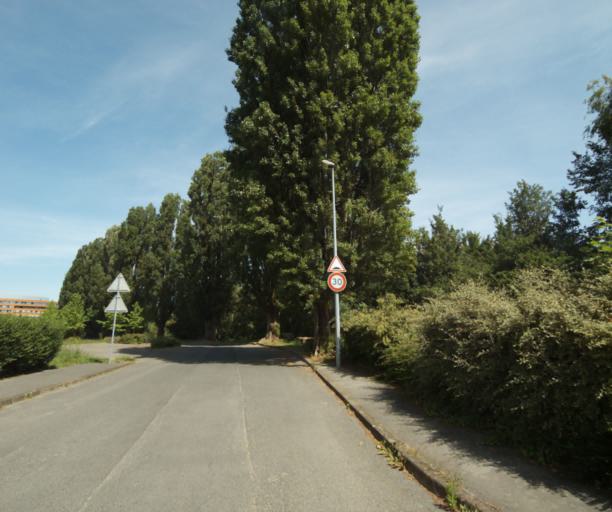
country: FR
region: Champagne-Ardenne
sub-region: Departement des Ardennes
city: Prix-les-Mezieres
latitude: 49.7602
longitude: 4.6920
